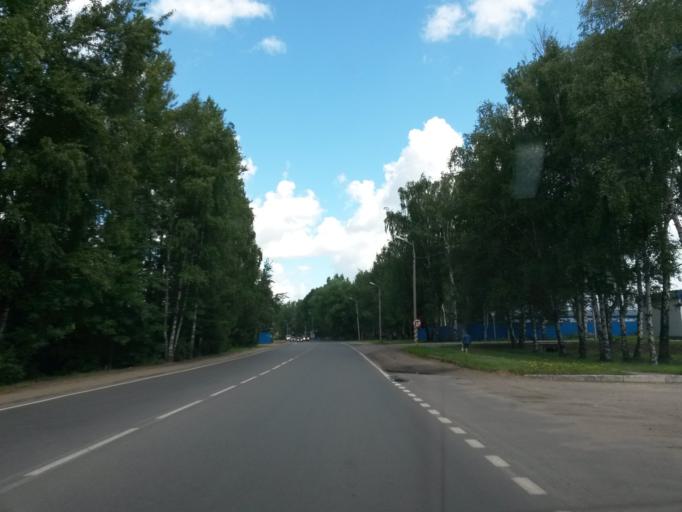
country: RU
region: Jaroslavl
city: Yaroslavl
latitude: 57.6541
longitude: 39.9078
